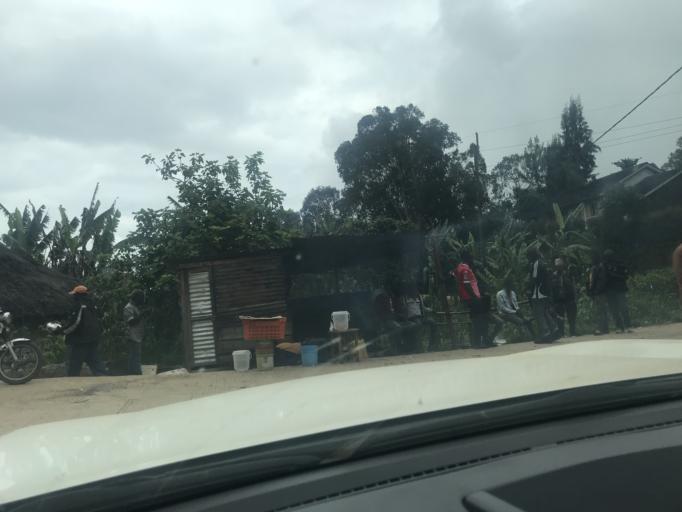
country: TZ
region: Morogoro
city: Morogoro
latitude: -7.0847
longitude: 37.5780
